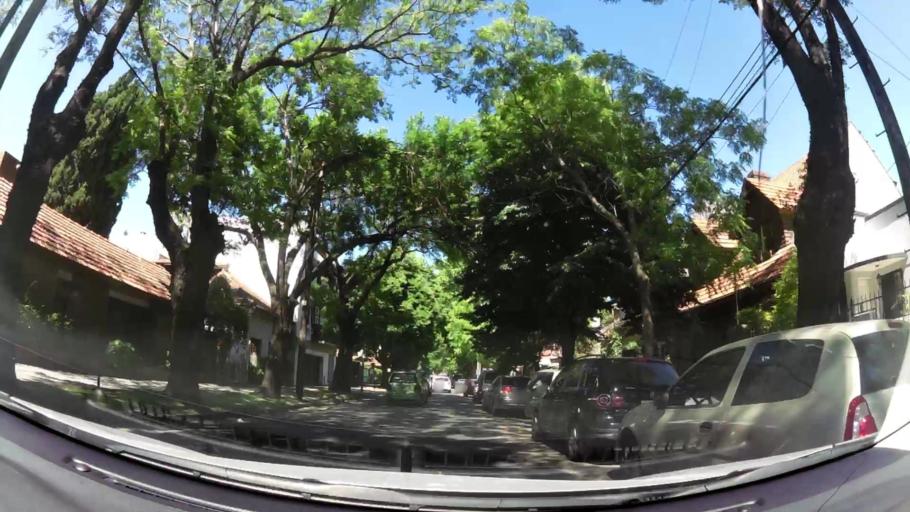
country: AR
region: Buenos Aires
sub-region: Partido de Vicente Lopez
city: Olivos
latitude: -34.5338
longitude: -58.4967
